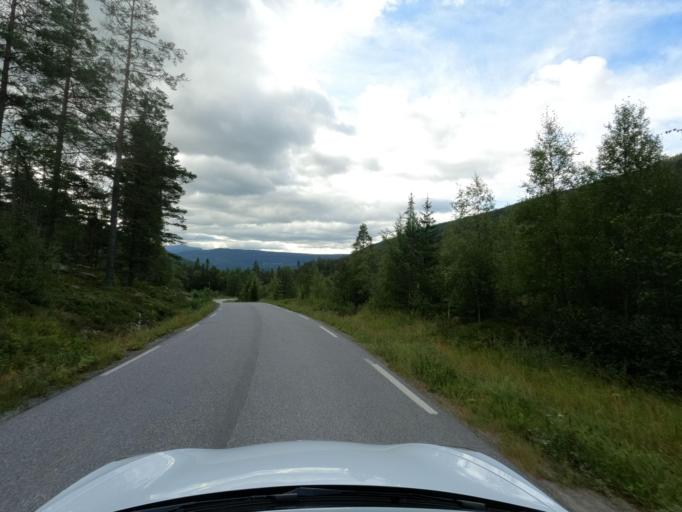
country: NO
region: Telemark
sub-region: Tinn
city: Rjukan
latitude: 60.0345
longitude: 8.7352
